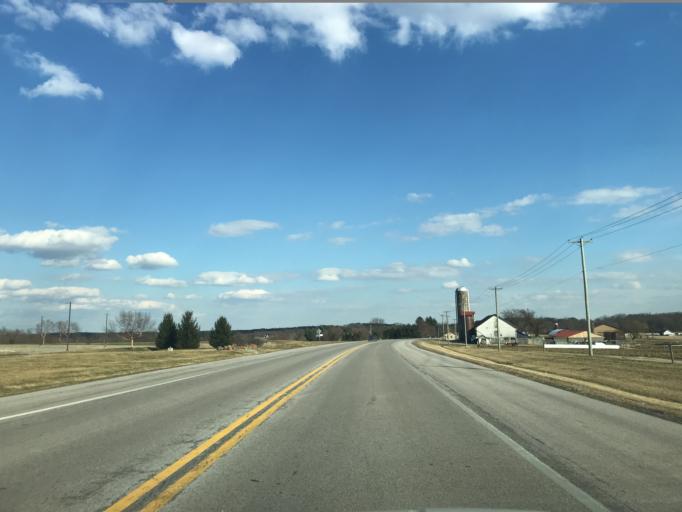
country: US
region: Maryland
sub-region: Cecil County
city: Rising Sun
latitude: 39.6616
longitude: -76.0041
